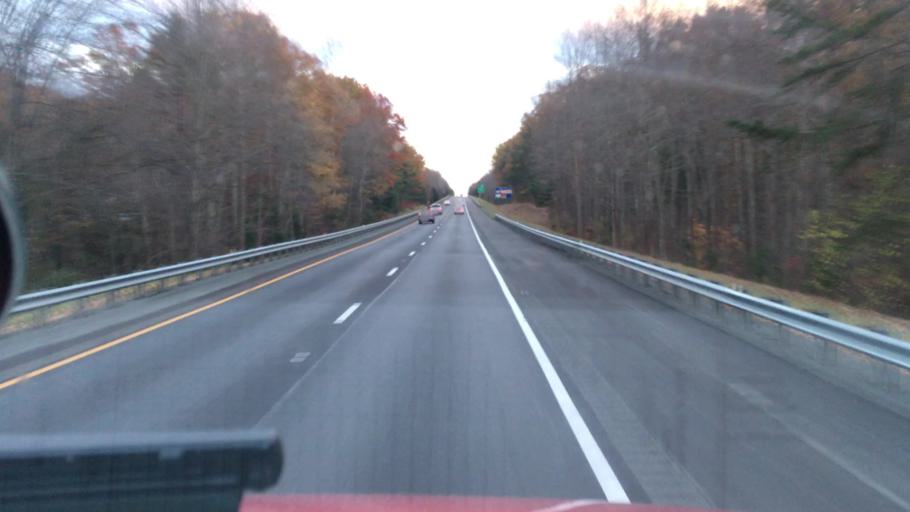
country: US
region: Virginia
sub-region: Fluvanna County
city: Lake Monticello
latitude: 37.9880
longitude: -78.2398
